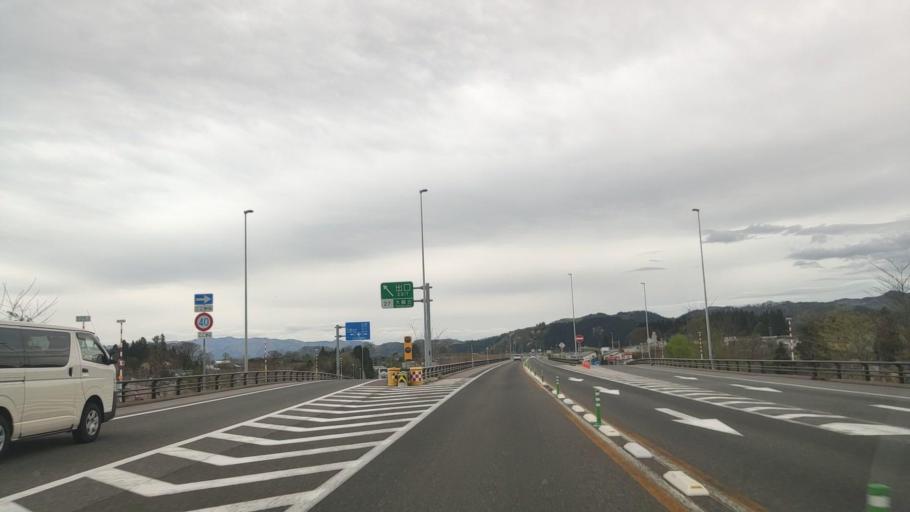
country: JP
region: Akita
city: Odate
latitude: 40.3052
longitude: 140.5685
